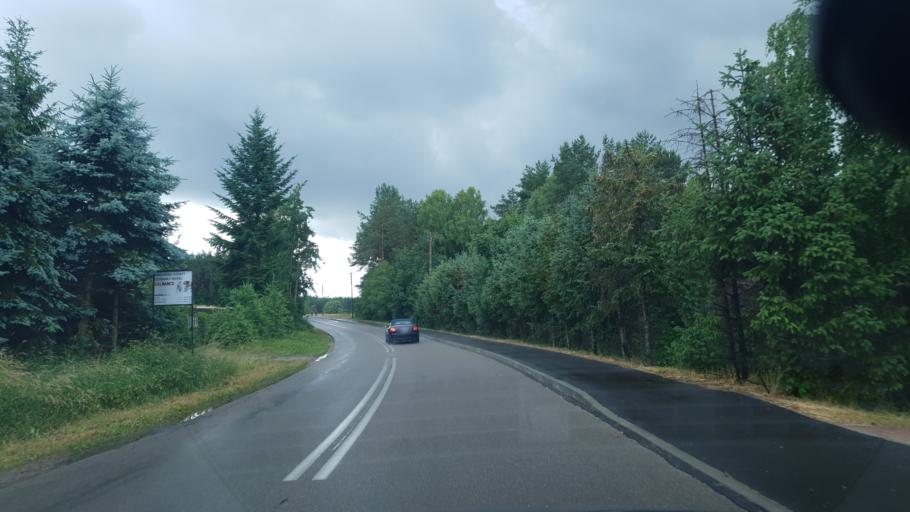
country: PL
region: Pomeranian Voivodeship
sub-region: Powiat kartuski
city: Stezyca
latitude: 54.2281
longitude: 17.9741
